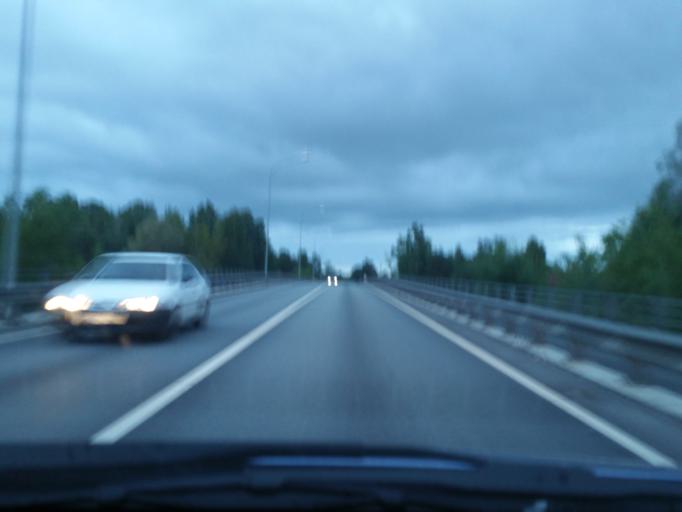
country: LV
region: Adazi
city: Adazi
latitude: 57.1207
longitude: 24.3256
